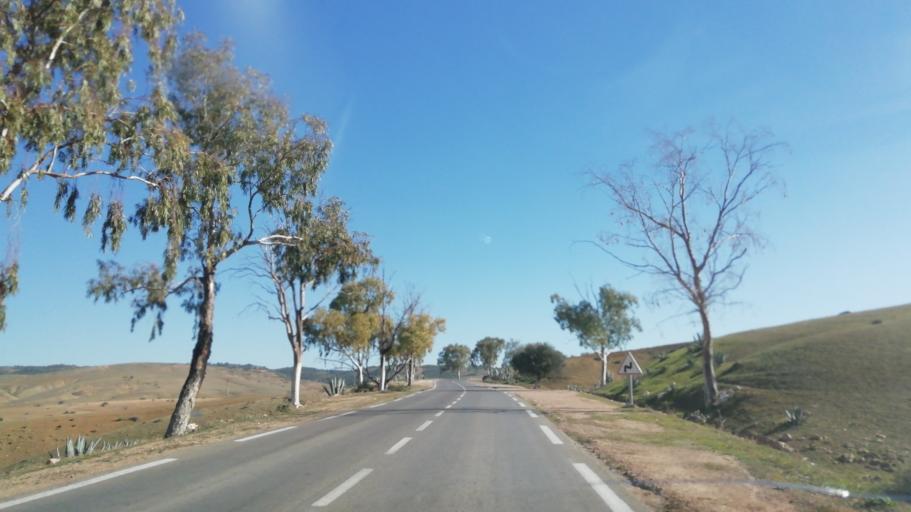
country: DZ
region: Tlemcen
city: Nedroma
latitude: 34.8283
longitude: -1.6423
